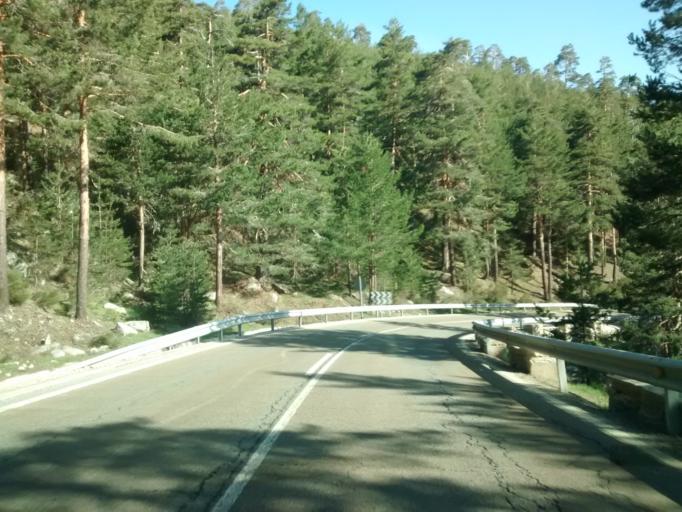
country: ES
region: Madrid
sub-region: Provincia de Madrid
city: Navacerrada
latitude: 40.8009
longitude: -4.0074
